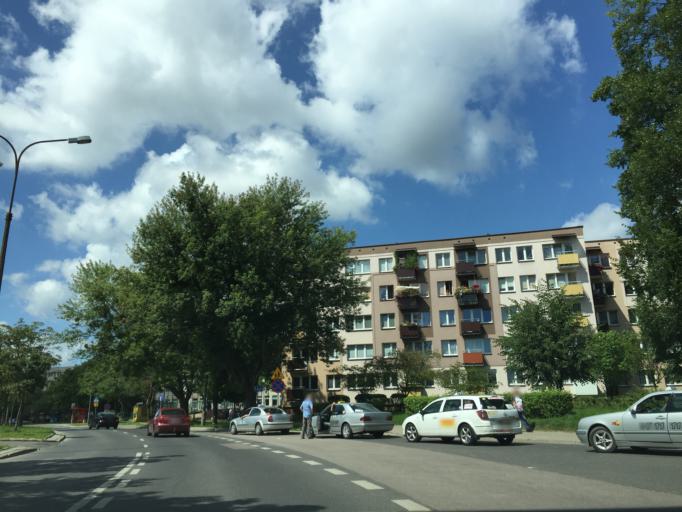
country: PL
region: Podlasie
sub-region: Bialystok
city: Bialystok
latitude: 53.1348
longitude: 23.1896
